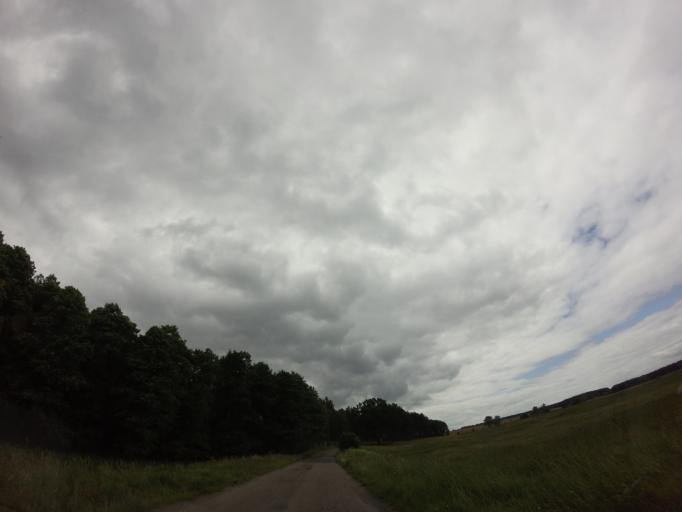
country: PL
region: West Pomeranian Voivodeship
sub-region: Powiat stargardzki
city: Insko
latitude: 53.4000
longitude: 15.5991
